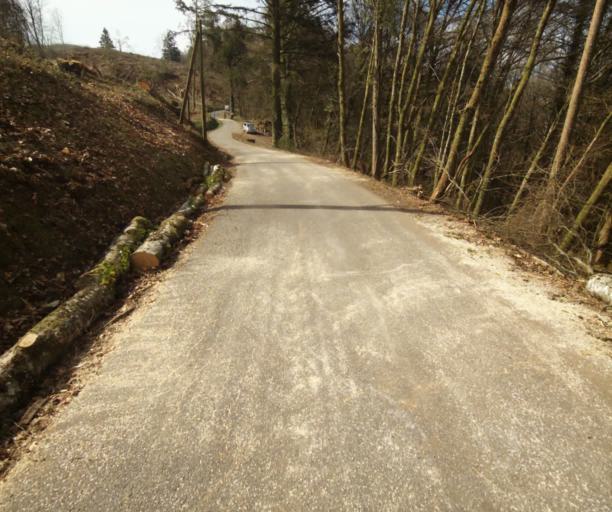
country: FR
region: Limousin
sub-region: Departement de la Correze
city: Correze
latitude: 45.3598
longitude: 1.8684
